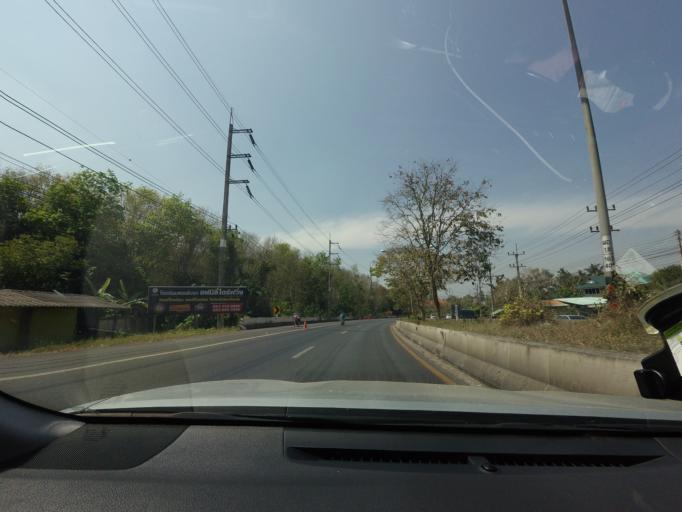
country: TH
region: Surat Thani
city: Kanchanadit
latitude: 9.1491
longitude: 99.4141
